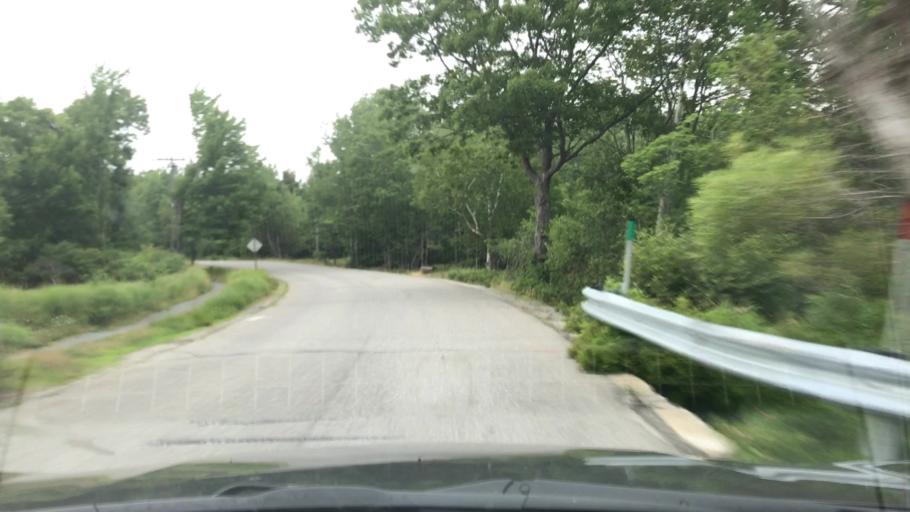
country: US
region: Maine
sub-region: Hancock County
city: Bar Harbor
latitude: 44.3426
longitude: -68.1795
